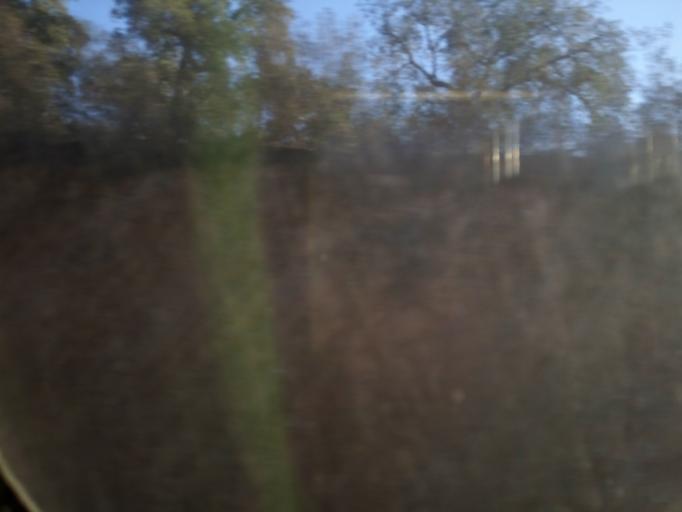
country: PT
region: Beja
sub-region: Ourique
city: Ourique
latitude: 37.6922
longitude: -8.4060
